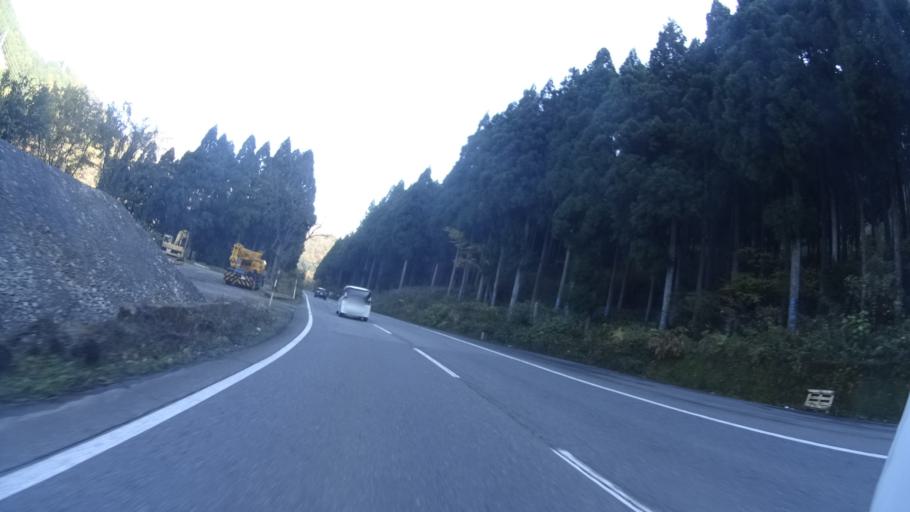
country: JP
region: Fukui
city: Ono
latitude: 35.9663
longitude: 136.5802
